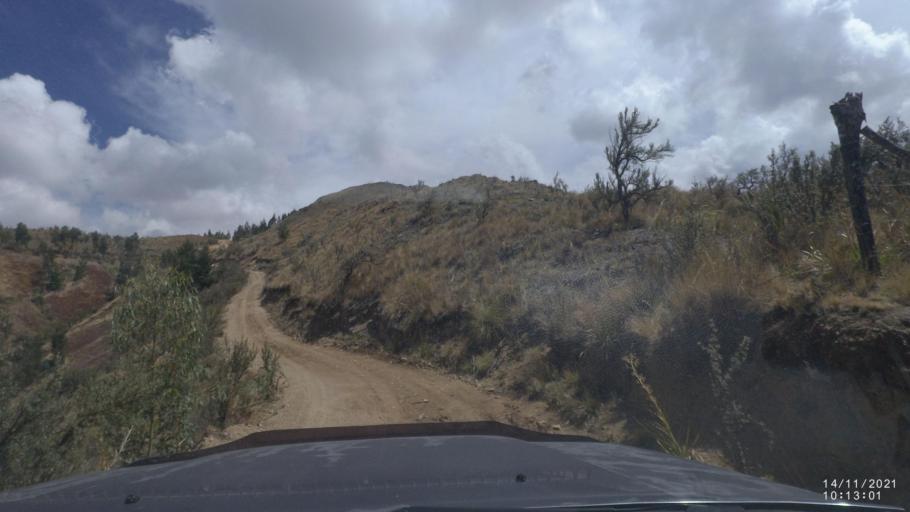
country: BO
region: Cochabamba
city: Cochabamba
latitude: -17.3448
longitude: -66.0860
